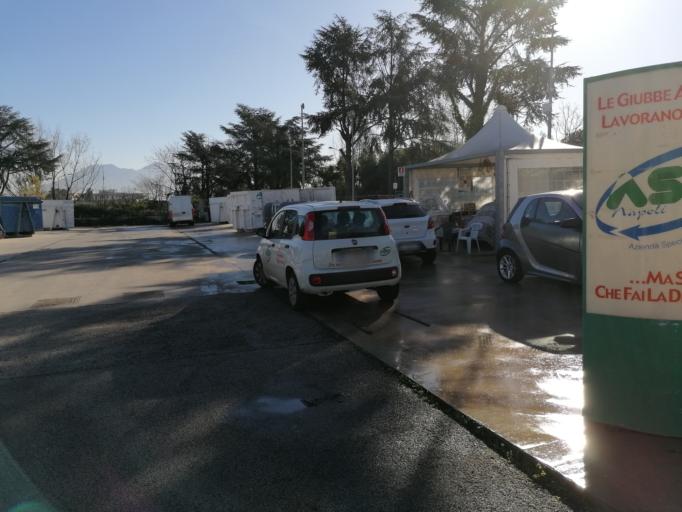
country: IT
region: Campania
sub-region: Provincia di Napoli
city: Casavatore
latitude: 40.8837
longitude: 14.2620
